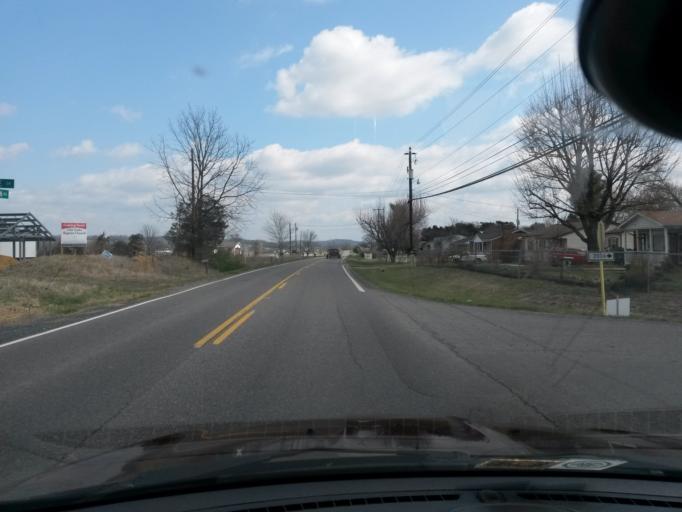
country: US
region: Virginia
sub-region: Augusta County
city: Weyers Cave
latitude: 38.2935
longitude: -78.9047
